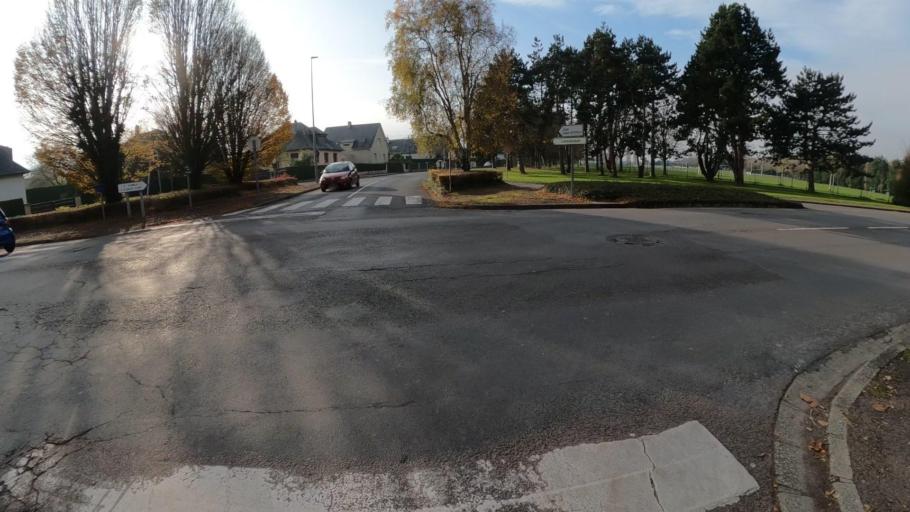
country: FR
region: Lower Normandy
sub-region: Departement du Calvados
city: Saint-Germain-la-Blanche-Herbe
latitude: 49.1941
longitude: -0.4023
